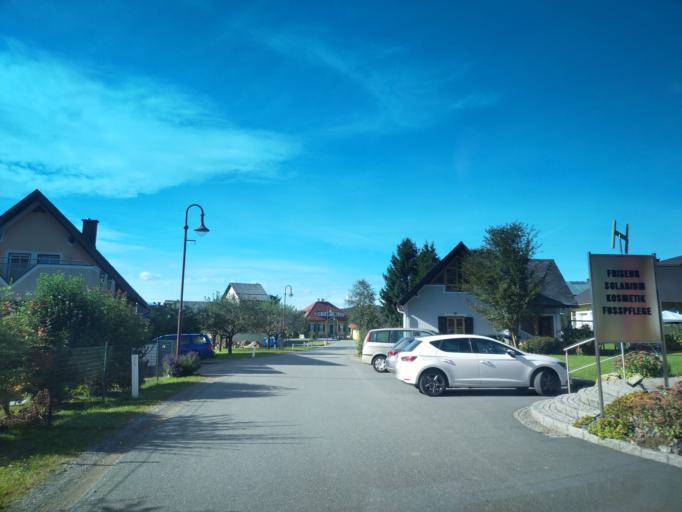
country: AT
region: Styria
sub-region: Politischer Bezirk Leibnitz
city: Sankt Johann im Saggautal
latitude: 46.6989
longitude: 15.4012
